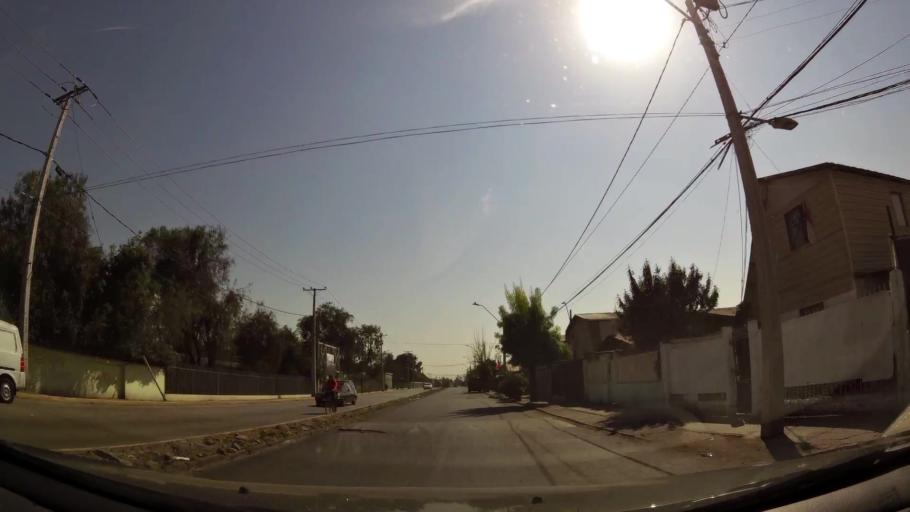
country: CL
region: Santiago Metropolitan
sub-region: Provincia de Maipo
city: San Bernardo
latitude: -33.5966
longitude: -70.6867
